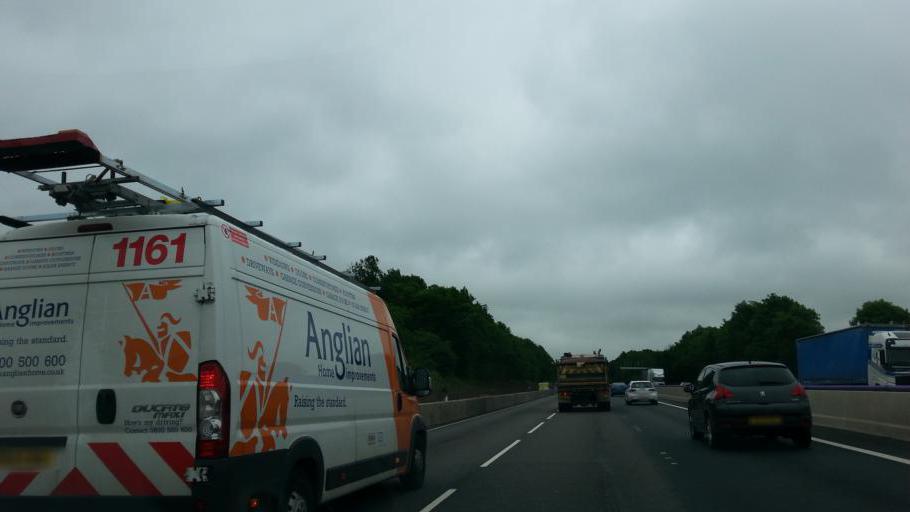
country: GB
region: England
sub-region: Northamptonshire
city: Long Buckby
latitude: 52.3413
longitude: -1.1515
